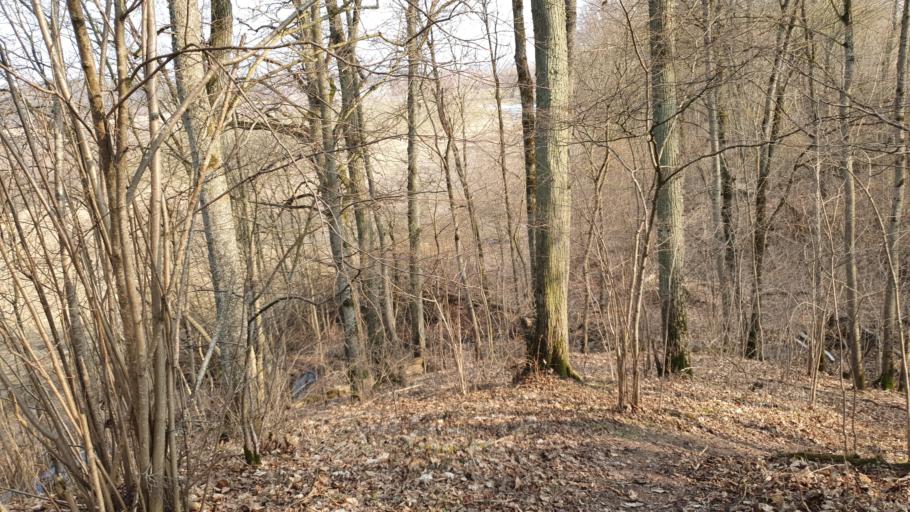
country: LV
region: Rundales
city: Pilsrundale
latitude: 56.4352
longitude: 24.0431
